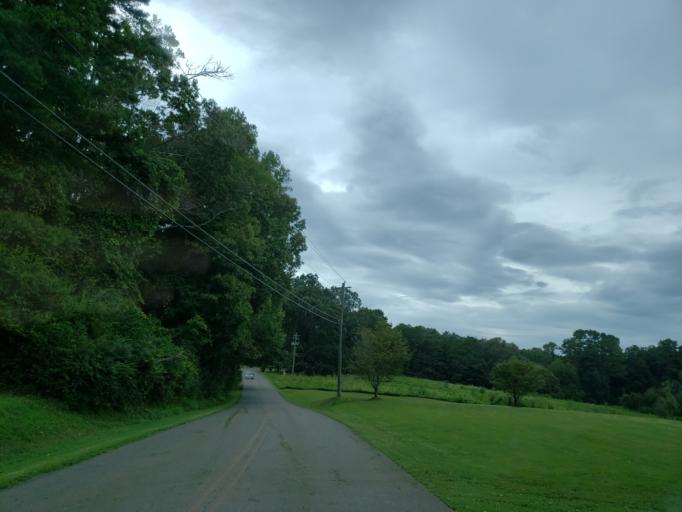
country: US
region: Georgia
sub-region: Gilmer County
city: Ellijay
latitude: 34.6453
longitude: -84.5026
